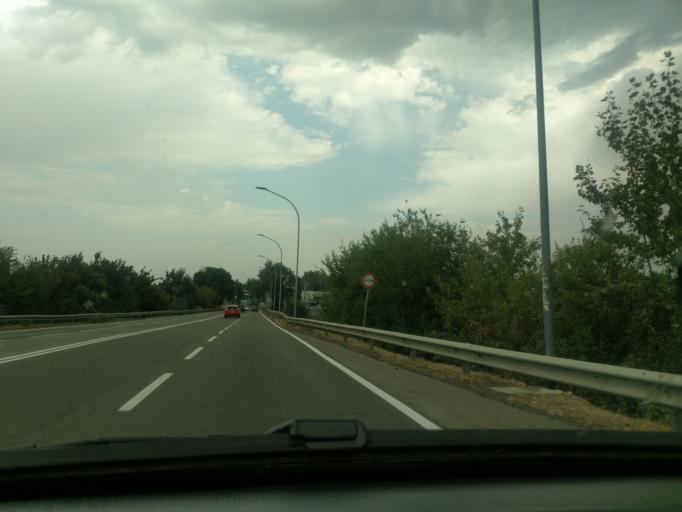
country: IT
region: Emilia-Romagna
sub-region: Provincia di Bologna
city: Calderara di Reno
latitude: 44.5298
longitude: 11.2661
